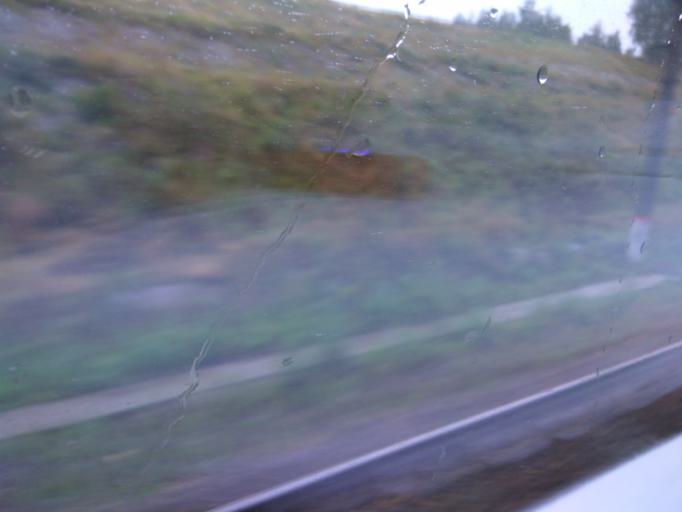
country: RU
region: Moskovskaya
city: Ozherel'ye
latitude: 54.8140
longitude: 38.2687
